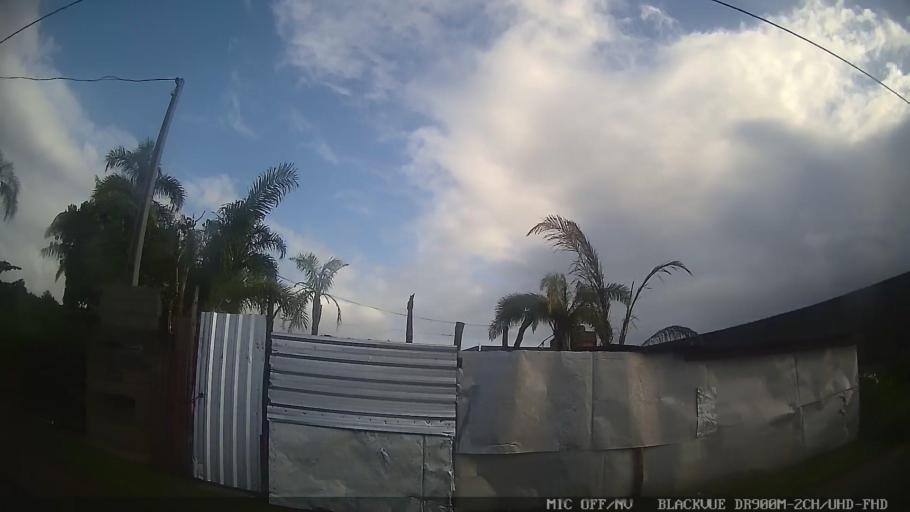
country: BR
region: Sao Paulo
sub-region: Itanhaem
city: Itanhaem
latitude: -24.2363
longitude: -46.8876
